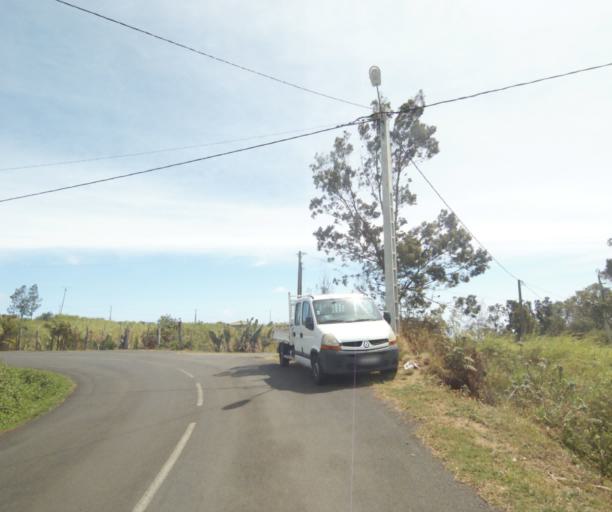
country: RE
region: Reunion
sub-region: Reunion
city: Trois-Bassins
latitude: -21.0679
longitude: 55.3081
